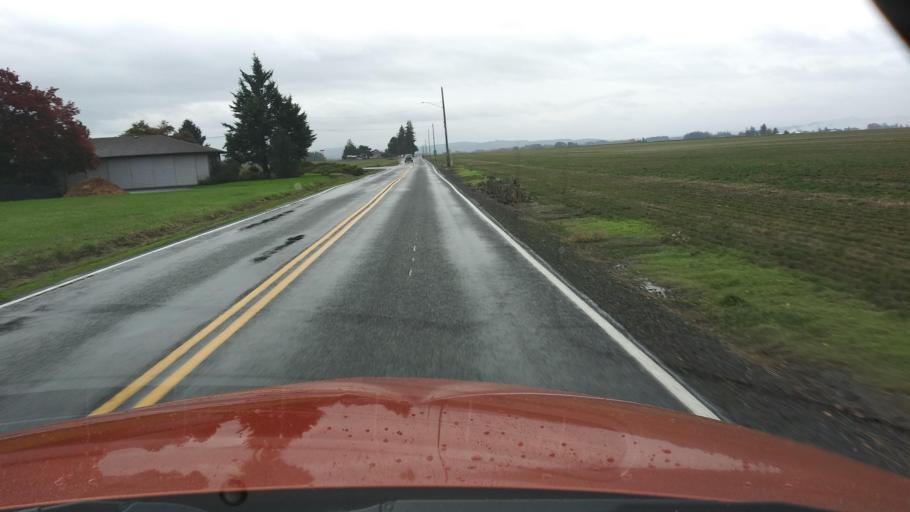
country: US
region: Oregon
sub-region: Washington County
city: North Plains
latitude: 45.5907
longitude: -123.0158
